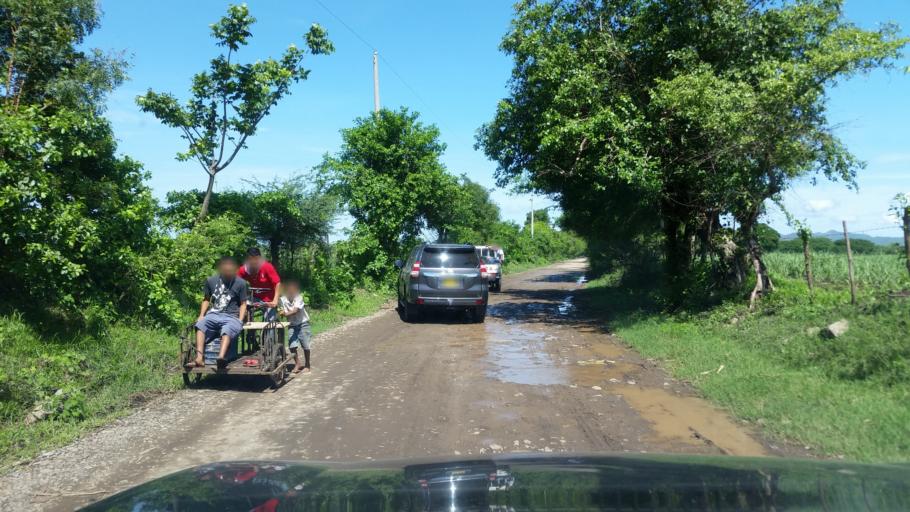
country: NI
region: Chinandega
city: Puerto Morazan
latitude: 12.7733
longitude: -87.1203
